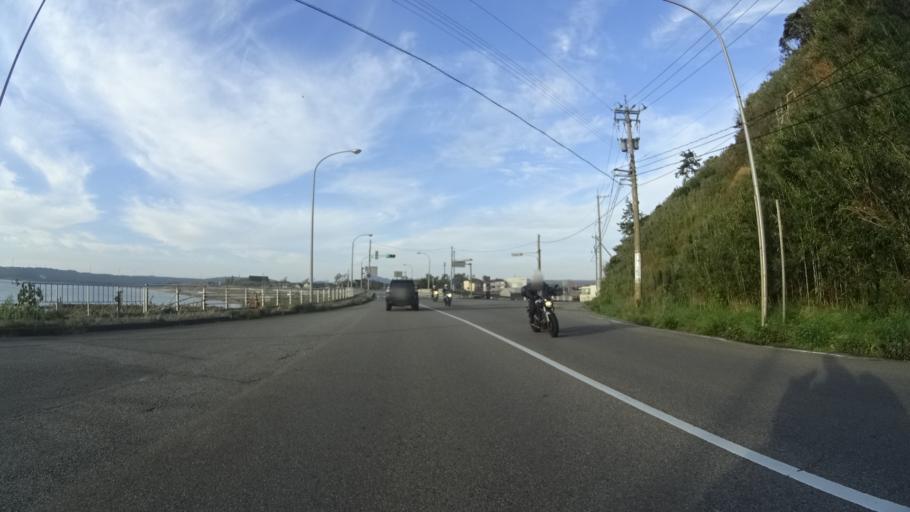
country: JP
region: Ishikawa
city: Nanao
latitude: 37.1339
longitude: 136.7279
